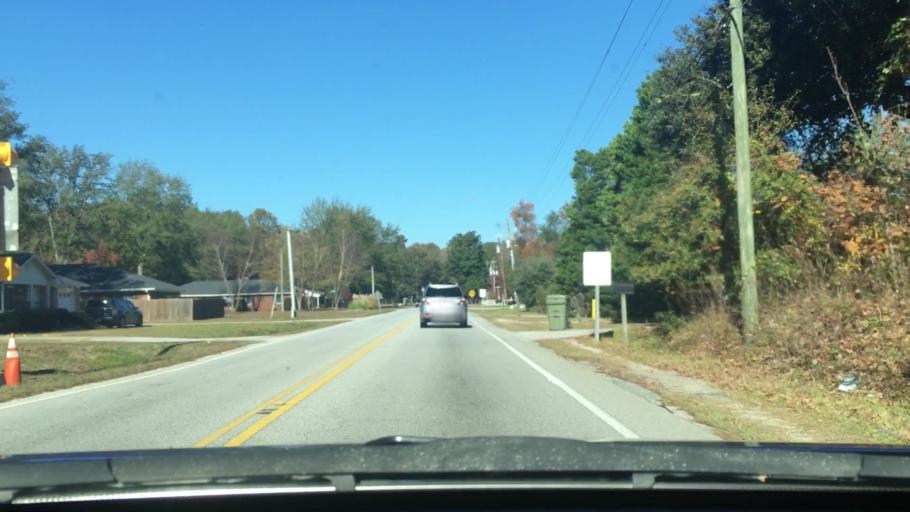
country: US
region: South Carolina
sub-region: Sumter County
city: South Sumter
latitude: 33.8923
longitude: -80.3674
